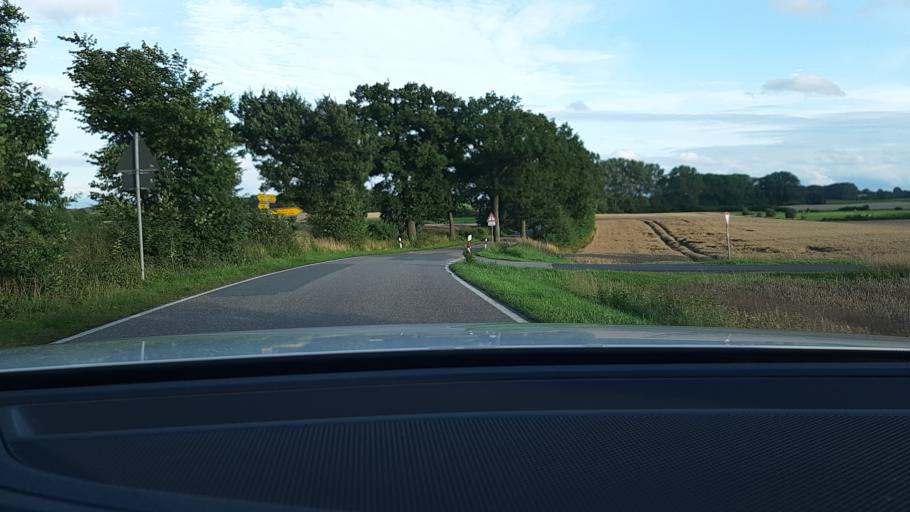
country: DE
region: Schleswig-Holstein
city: Stockelsdorf
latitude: 53.9184
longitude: 10.6224
